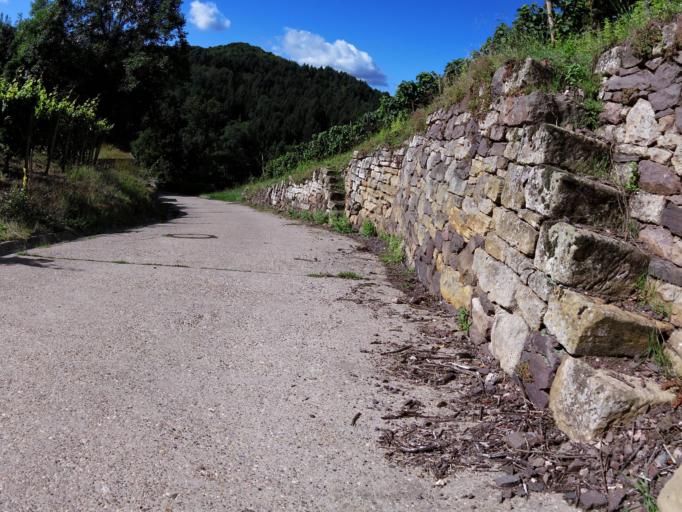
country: DE
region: Rheinland-Pfalz
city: Schlossbockelheim
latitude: 49.8040
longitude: 7.7418
